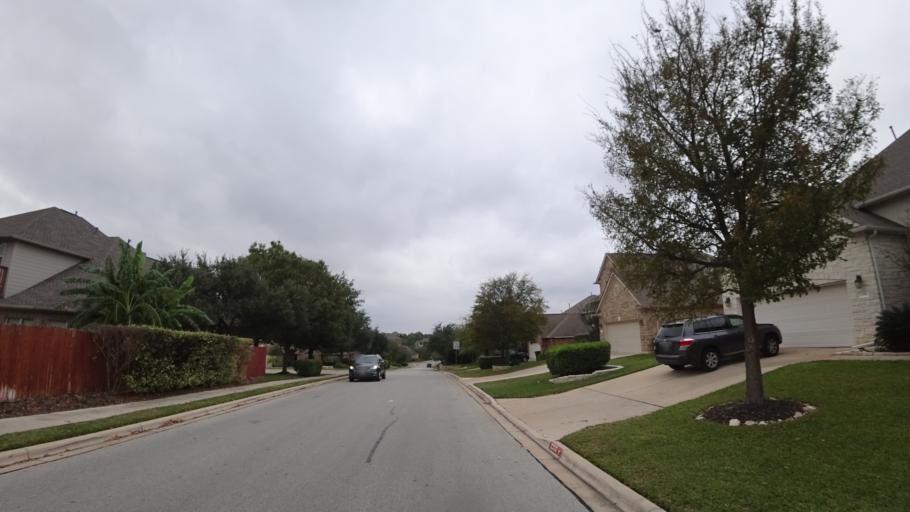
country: US
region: Texas
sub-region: Travis County
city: Hudson Bend
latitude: 30.3617
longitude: -97.8994
